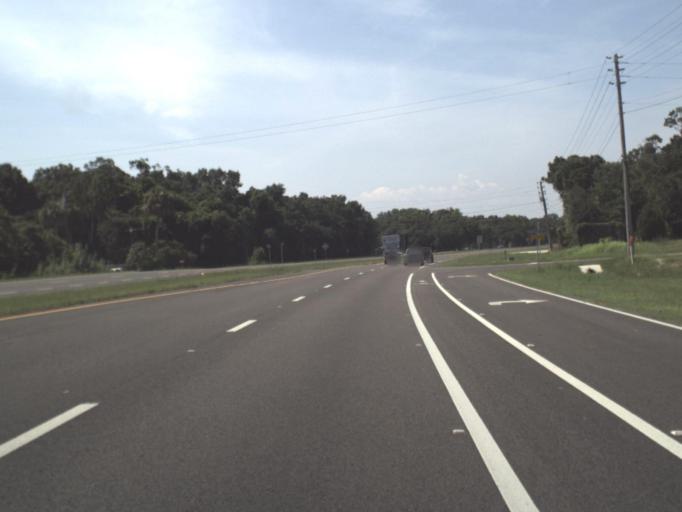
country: US
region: Florida
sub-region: Levy County
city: Inglis
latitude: 29.0205
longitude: -82.6684
